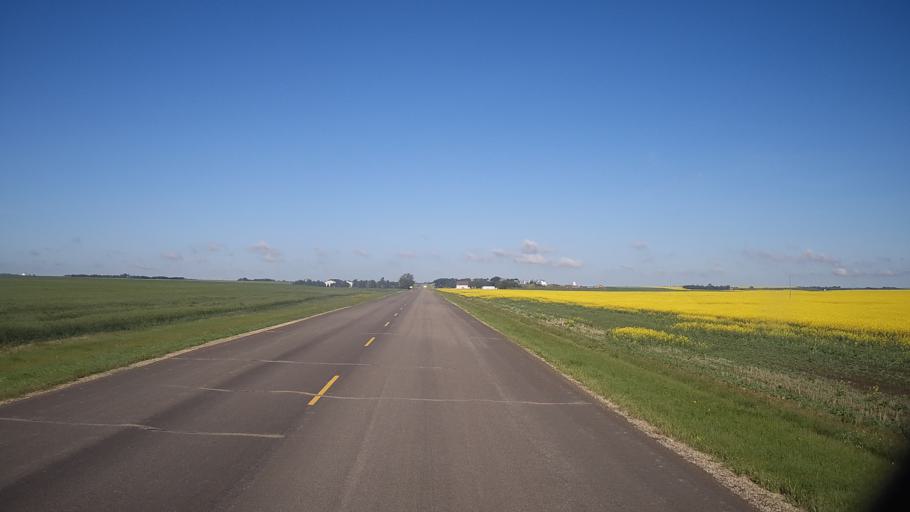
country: CA
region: Saskatchewan
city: Watrous
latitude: 51.6780
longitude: -105.3894
